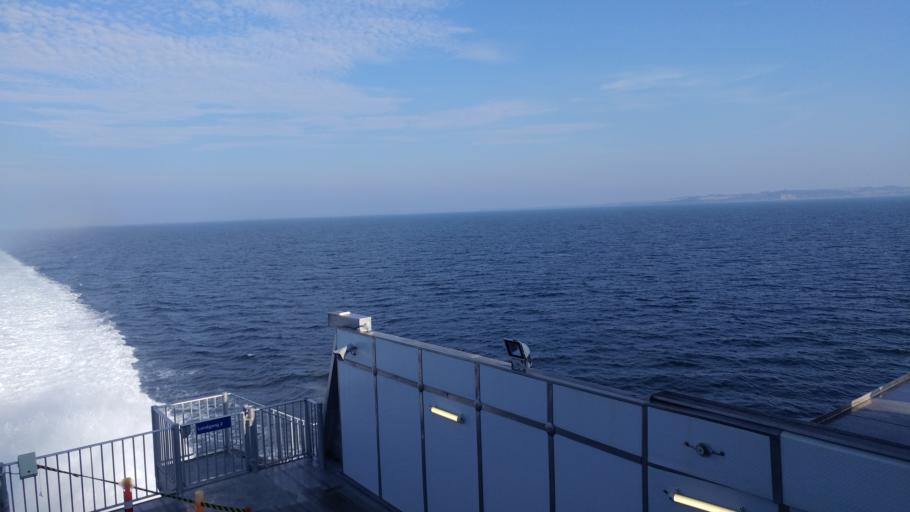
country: DK
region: Central Jutland
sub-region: Arhus Kommune
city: Logten
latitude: 56.1129
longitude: 10.3927
